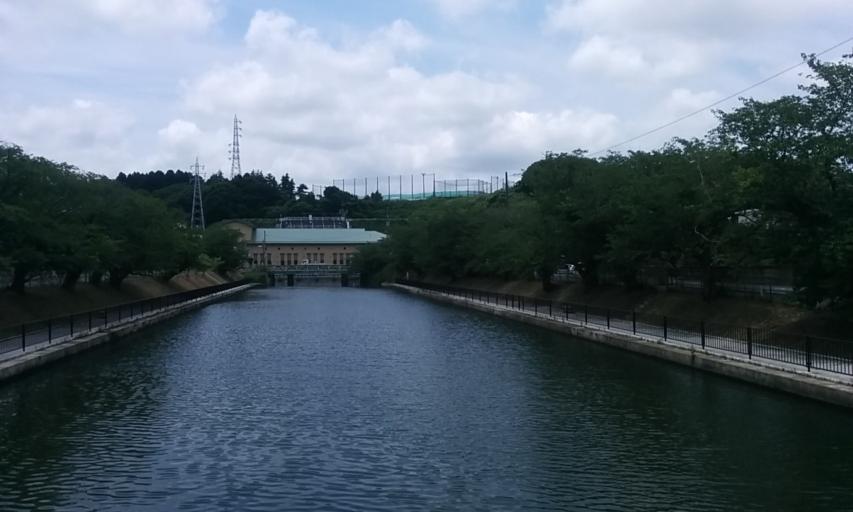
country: JP
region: Chiba
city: Katori-shi
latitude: 35.8978
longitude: 140.4894
